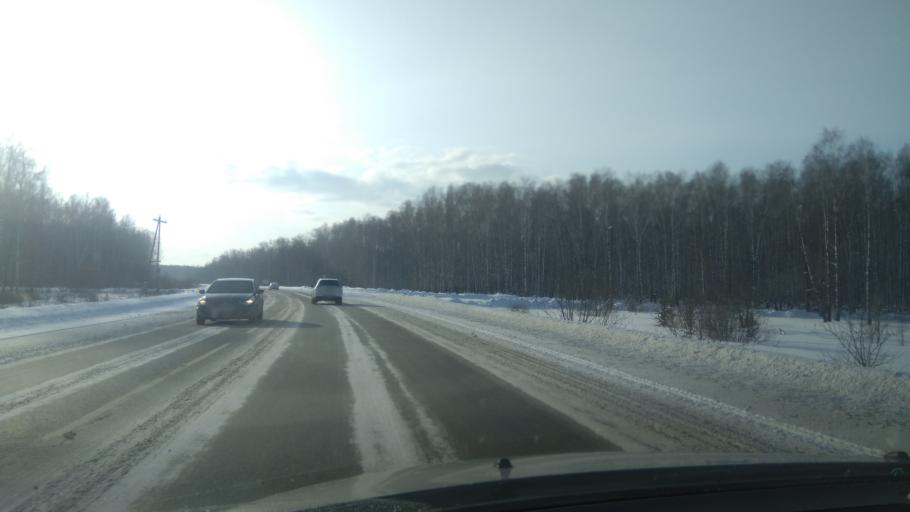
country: RU
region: Sverdlovsk
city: Bogdanovich
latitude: 56.7952
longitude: 62.0035
